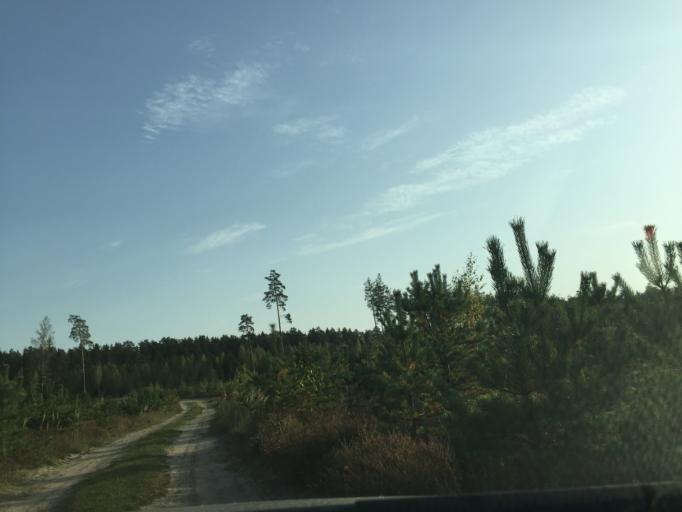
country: LV
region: Garkalne
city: Garkalne
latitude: 56.9685
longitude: 24.4209
